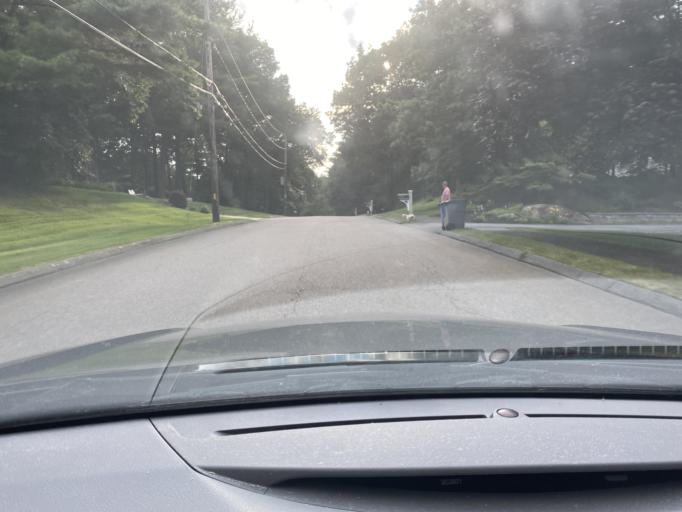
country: US
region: Massachusetts
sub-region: Norfolk County
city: Walpole
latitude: 42.1767
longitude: -71.2630
